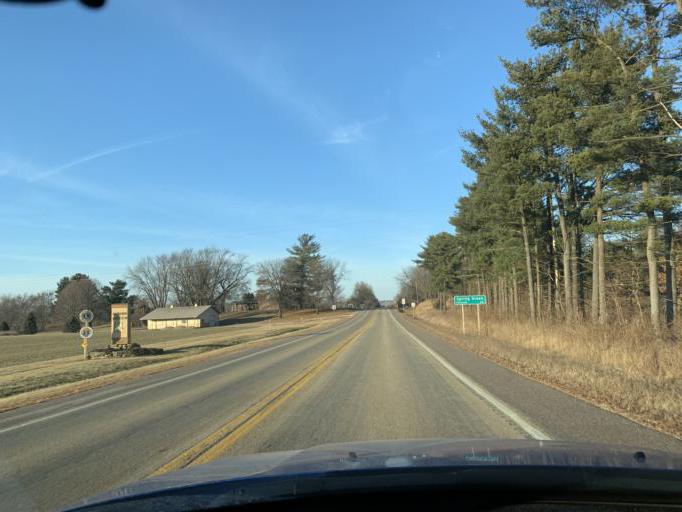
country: US
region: Wisconsin
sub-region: Sauk County
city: Spring Green
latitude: 43.1669
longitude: -90.0640
